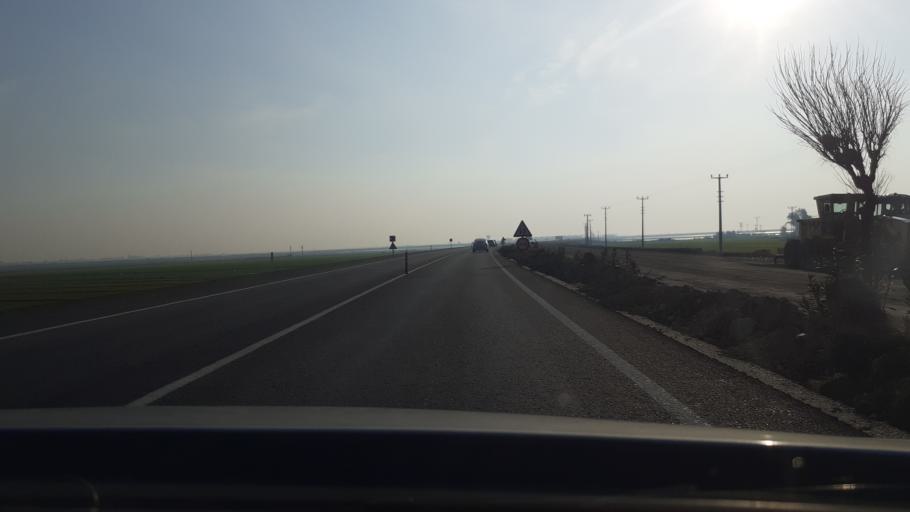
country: TR
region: Hatay
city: Serinyol
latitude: 36.3709
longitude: 36.2509
